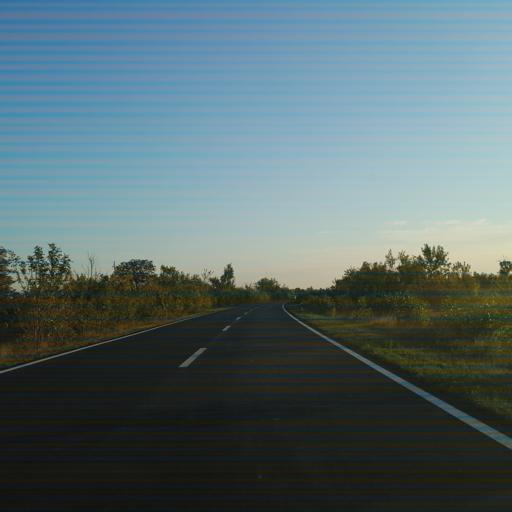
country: RS
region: Central Serbia
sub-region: Borski Okrug
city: Negotin
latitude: 44.1950
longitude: 22.3709
